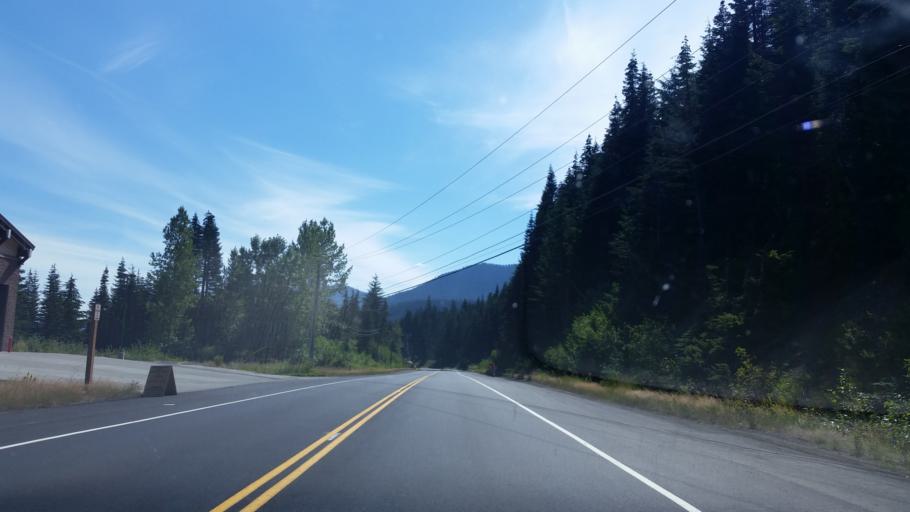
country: US
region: Washington
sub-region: King County
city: Tanner
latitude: 47.4175
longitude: -121.4131
